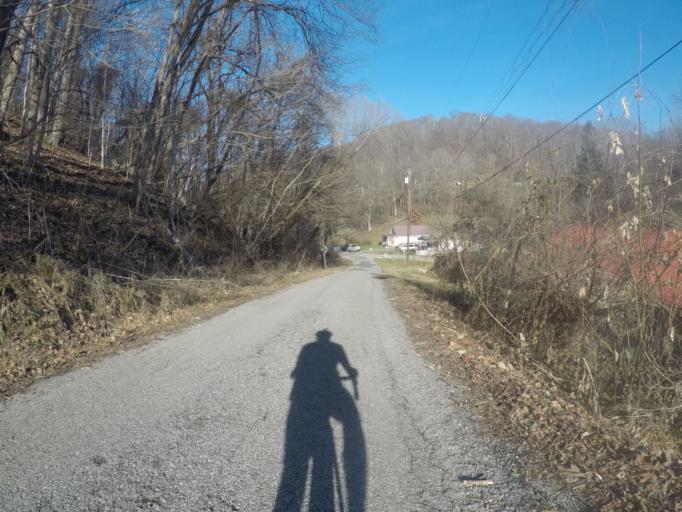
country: US
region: West Virginia
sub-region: Cabell County
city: Huntington
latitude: 38.3915
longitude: -82.4863
